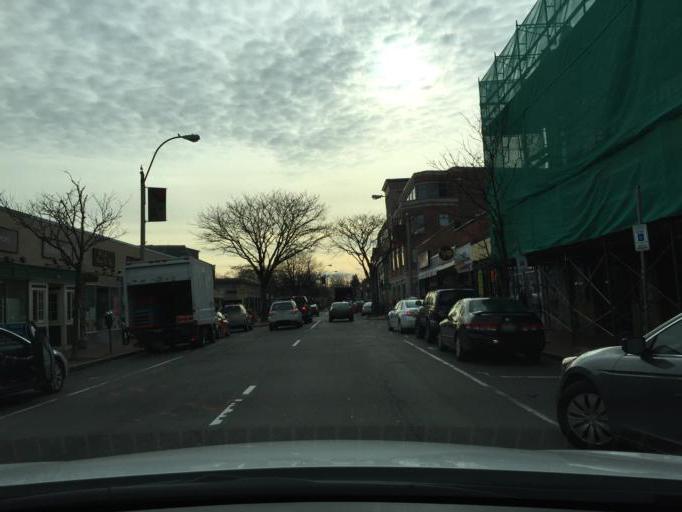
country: US
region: Massachusetts
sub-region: Middlesex County
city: Somerville
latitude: 42.3953
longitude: -71.1218
